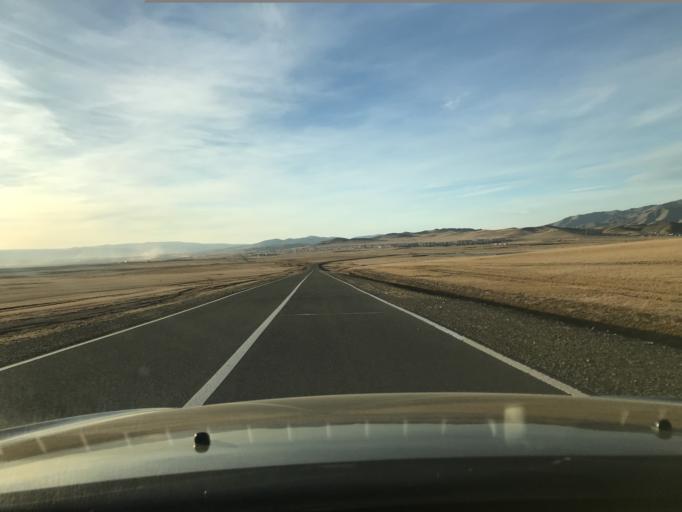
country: MN
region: Central Aimak
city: Arhust
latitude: 47.7647
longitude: 107.4298
